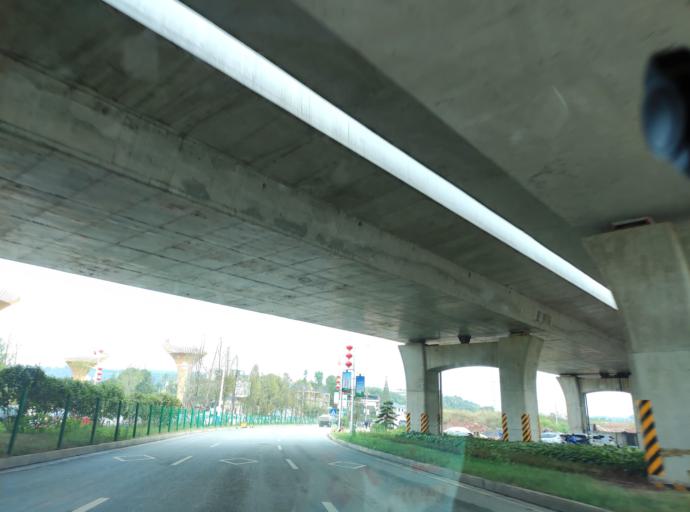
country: CN
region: Jiangxi Sheng
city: Pingxiang
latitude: 27.6622
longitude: 113.9100
